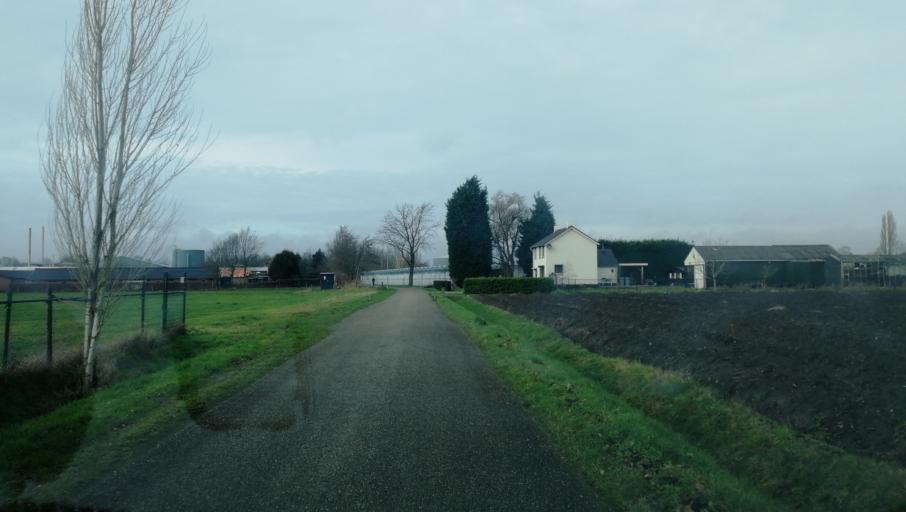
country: NL
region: Limburg
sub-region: Gemeente Beesel
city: Offenbeek
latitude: 51.2946
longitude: 6.1280
